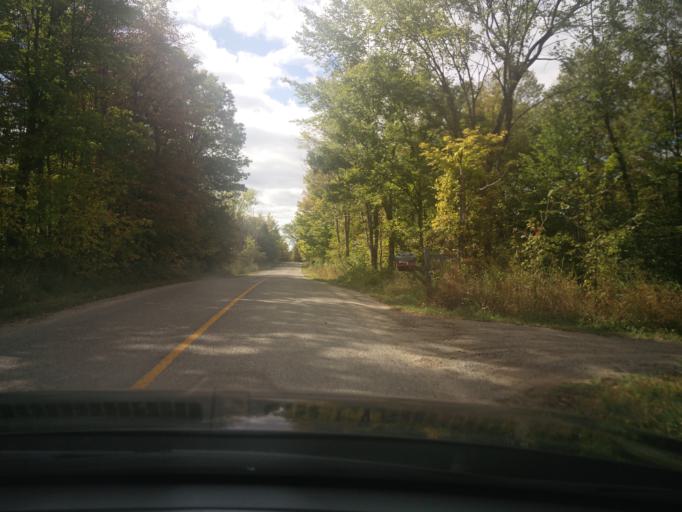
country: CA
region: Ontario
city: Perth
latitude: 44.6579
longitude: -76.5476
